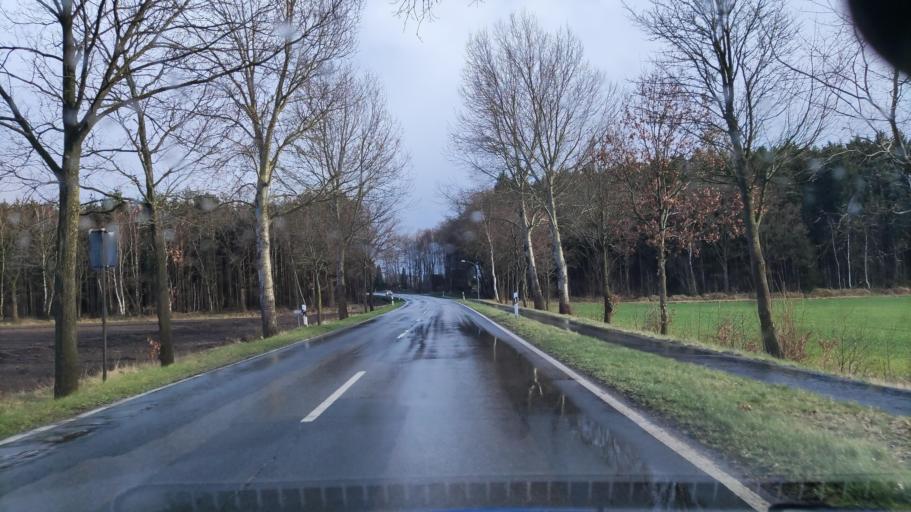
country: DE
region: Lower Saxony
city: Eschede
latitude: 52.7474
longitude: 10.2259
